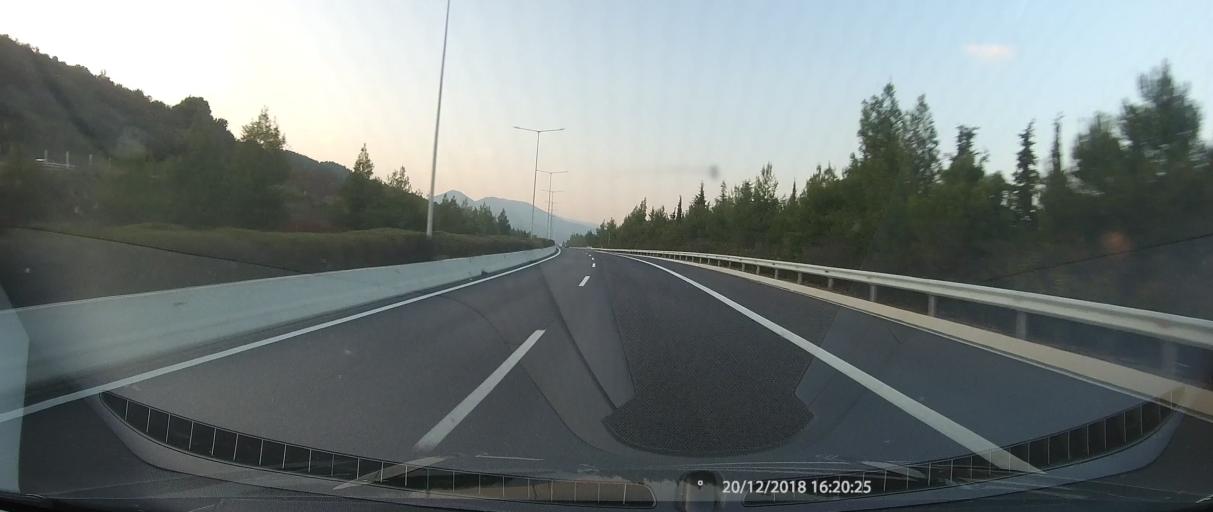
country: GR
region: Thessaly
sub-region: Nomos Magnisias
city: Pteleos
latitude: 39.0294
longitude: 22.9102
